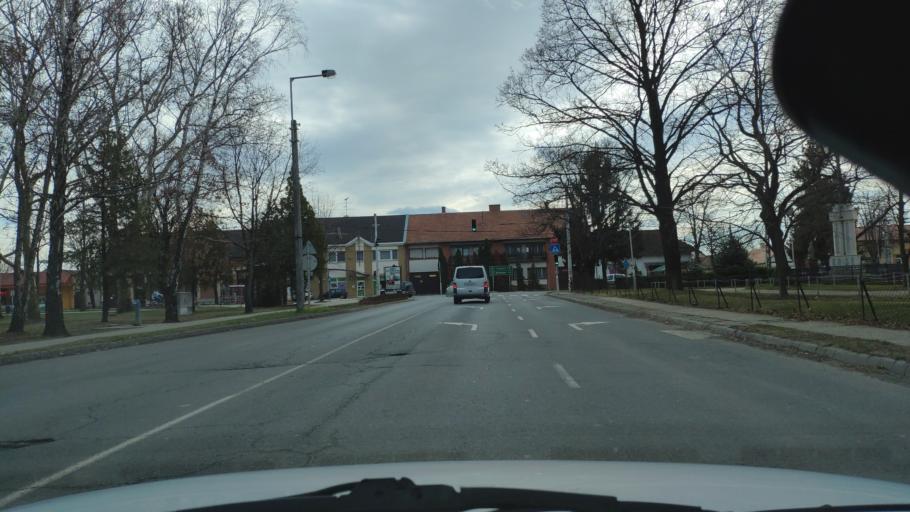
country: HU
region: Bacs-Kiskun
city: Lajosmizse
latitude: 47.0269
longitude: 19.5583
